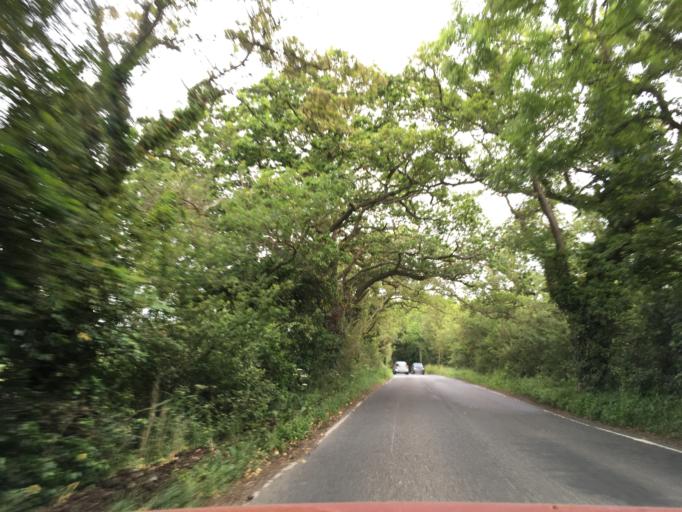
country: GB
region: England
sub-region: North Somerset
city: Portishead
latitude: 51.4707
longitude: -2.7639
